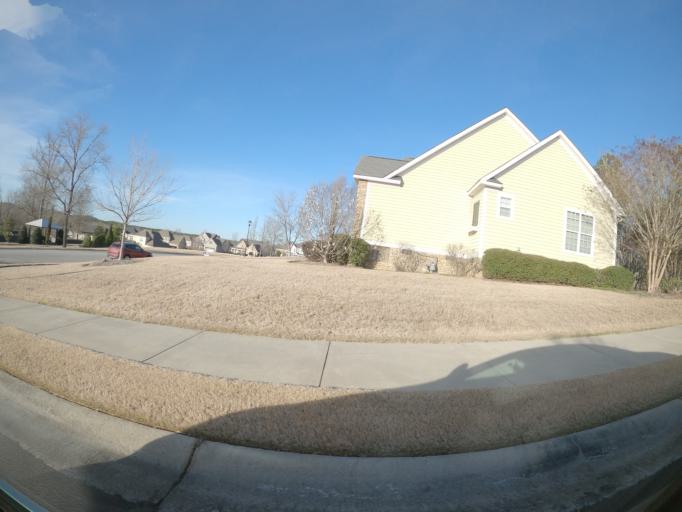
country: US
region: Georgia
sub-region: Columbia County
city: Evans
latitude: 33.5863
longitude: -82.1995
